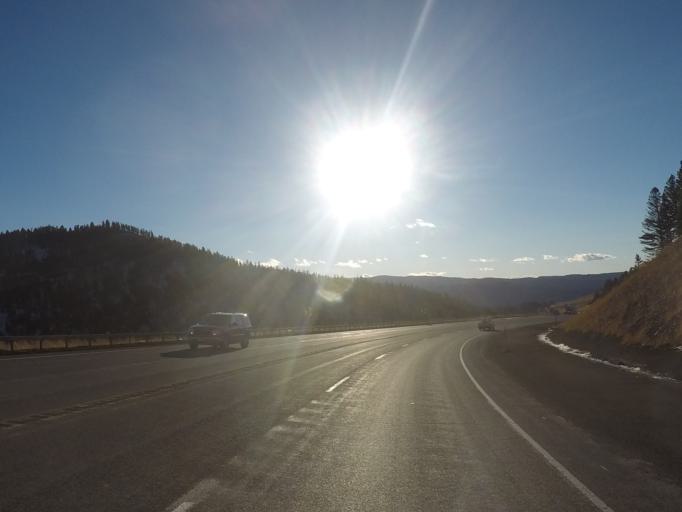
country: US
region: Montana
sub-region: Lewis and Clark County
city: Helena West Side
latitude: 46.5591
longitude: -112.3404
